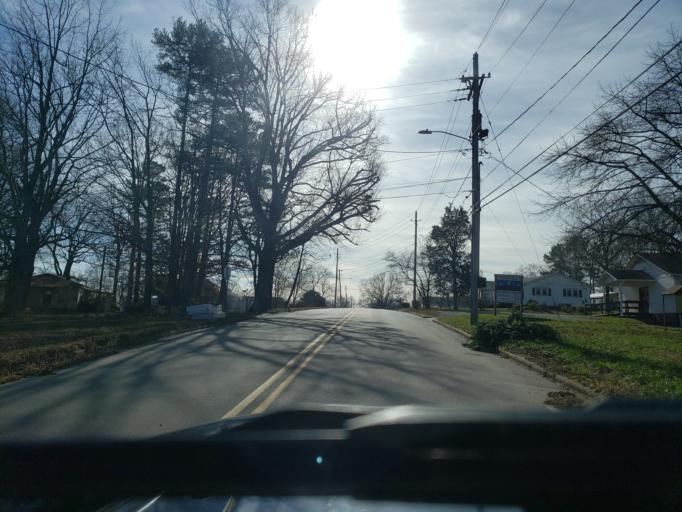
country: US
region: North Carolina
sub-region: Cleveland County
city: Kings Mountain
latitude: 35.2583
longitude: -81.3319
